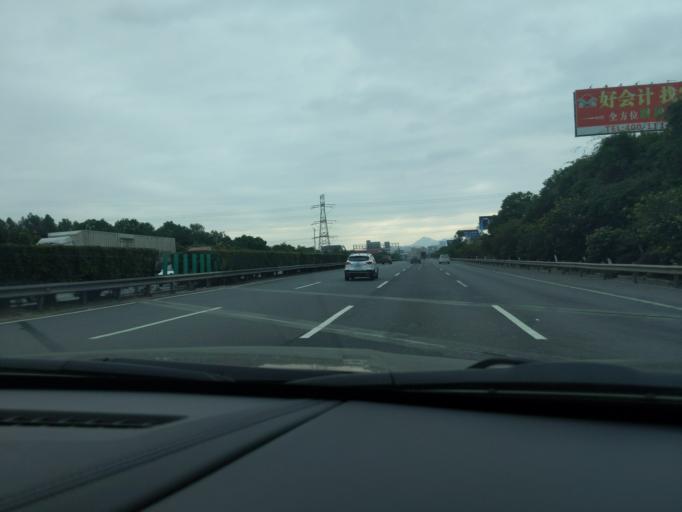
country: CN
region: Fujian
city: Neikeng
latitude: 24.7640
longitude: 118.4495
